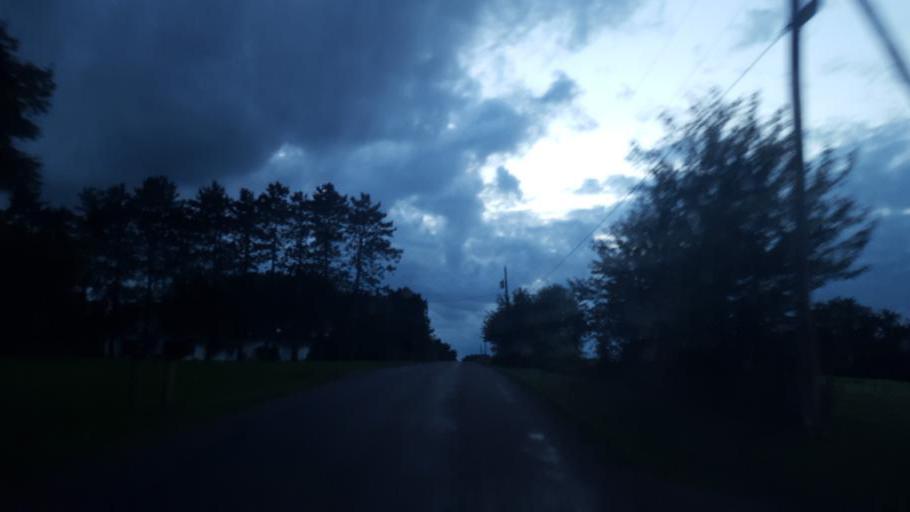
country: US
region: Ohio
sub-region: Richland County
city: Lexington
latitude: 40.6301
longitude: -82.5967
